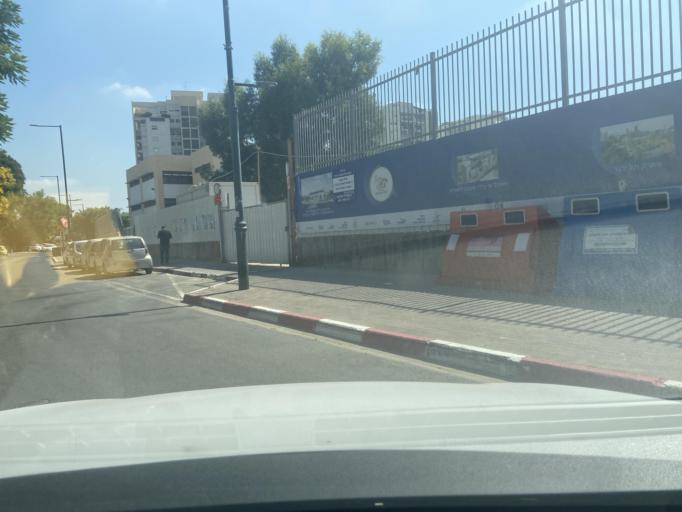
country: IL
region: Central District
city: Yehud
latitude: 32.0331
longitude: 34.8776
